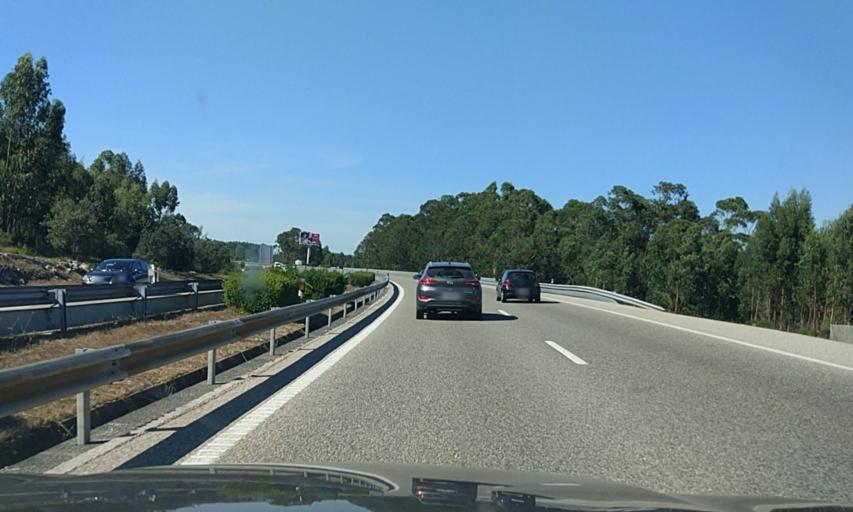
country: PT
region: Santarem
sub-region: Ourem
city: Fatima
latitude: 39.5624
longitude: -8.6593
